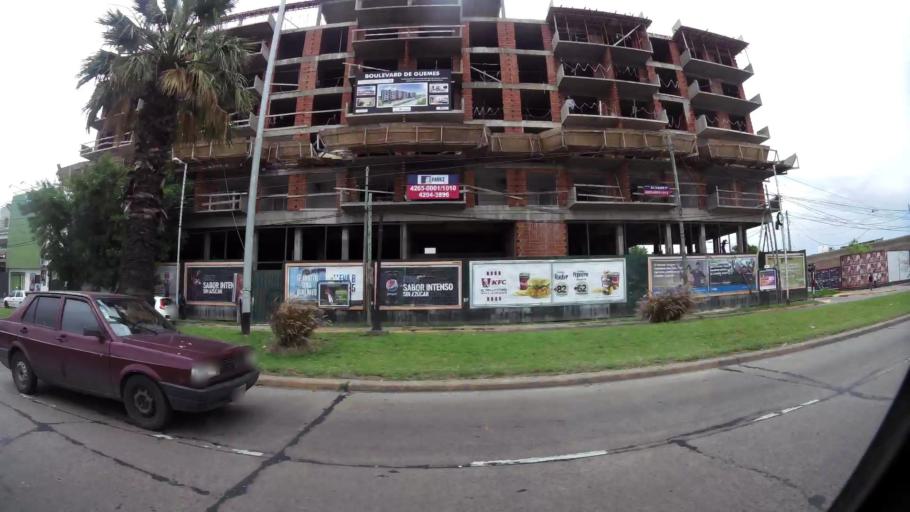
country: AR
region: Buenos Aires
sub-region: Partido de Avellaneda
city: Avellaneda
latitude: -34.6777
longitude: -58.3672
